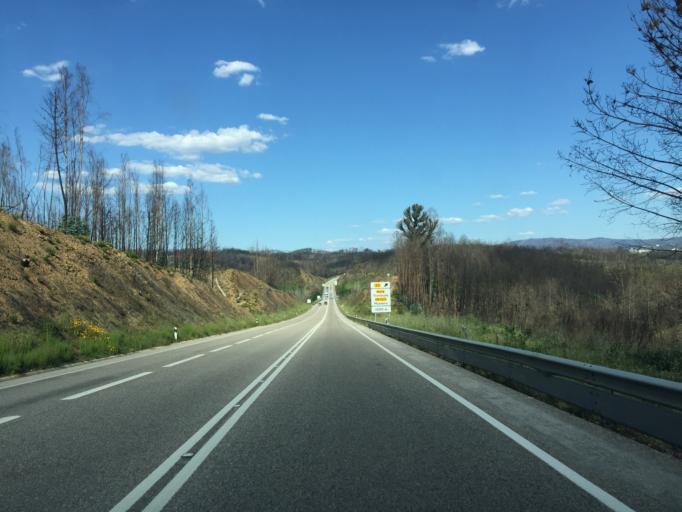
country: PT
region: Leiria
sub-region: Pedrogao Grande
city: Pedrogao Grande
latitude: 39.9260
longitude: -8.1978
